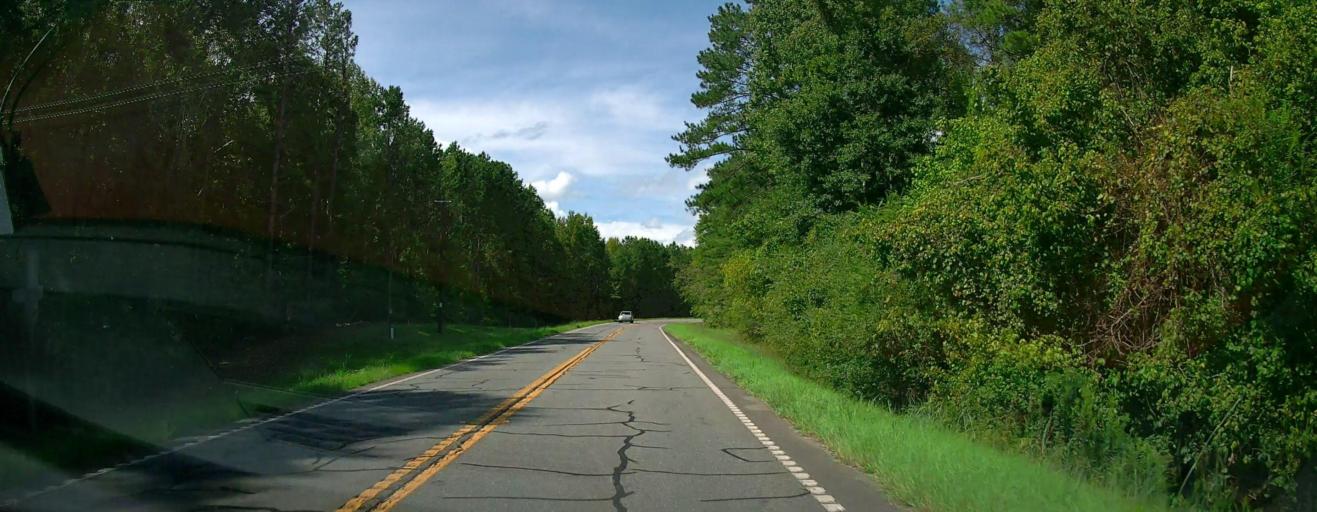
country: US
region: Georgia
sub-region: Talbot County
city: Talbotton
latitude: 32.7079
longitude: -84.5552
